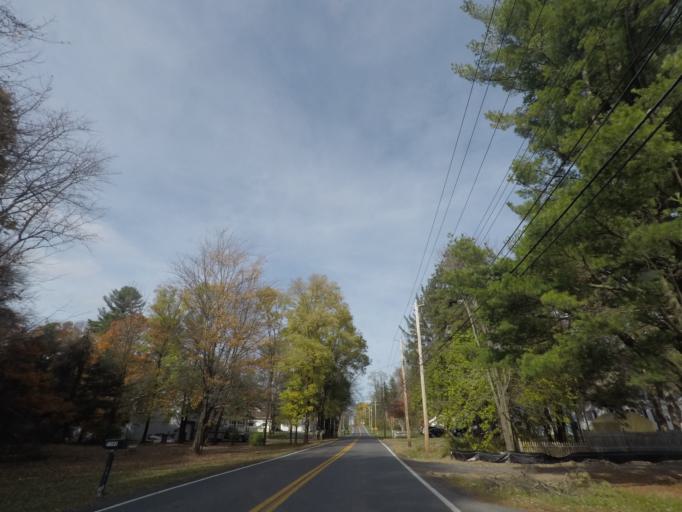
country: US
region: New York
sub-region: Schenectady County
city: Rotterdam
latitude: 42.7555
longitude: -73.9596
